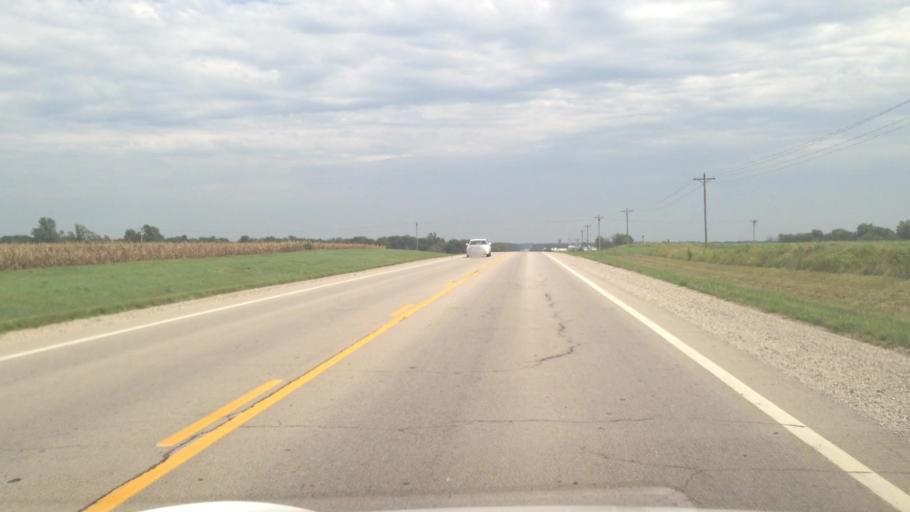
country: US
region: Kansas
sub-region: Crawford County
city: Girard
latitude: 37.5143
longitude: -94.9273
